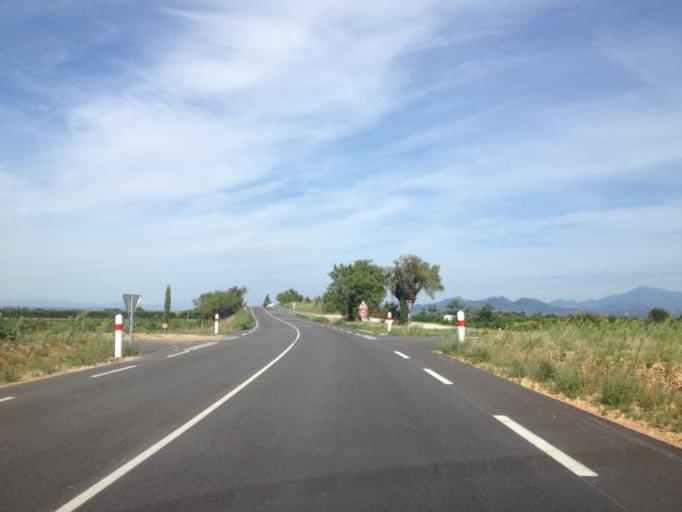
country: FR
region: Provence-Alpes-Cote d'Azur
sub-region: Departement du Vaucluse
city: Courthezon
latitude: 44.0993
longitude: 4.8616
